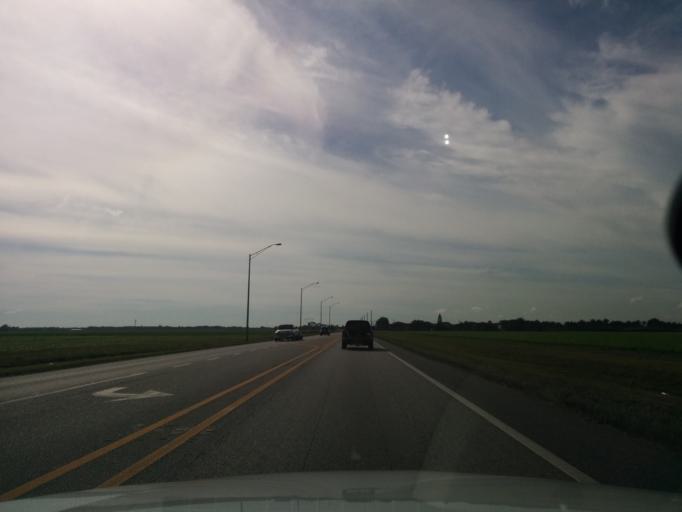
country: US
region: Florida
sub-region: Miami-Dade County
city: Country Walk
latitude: 25.6368
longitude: -80.4798
